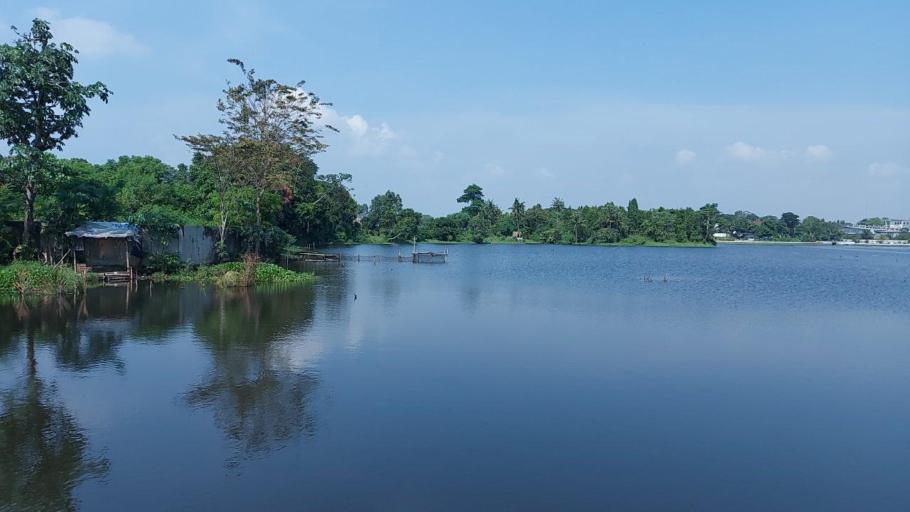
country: ID
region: West Java
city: Cibinong
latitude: -6.4696
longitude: 106.8585
